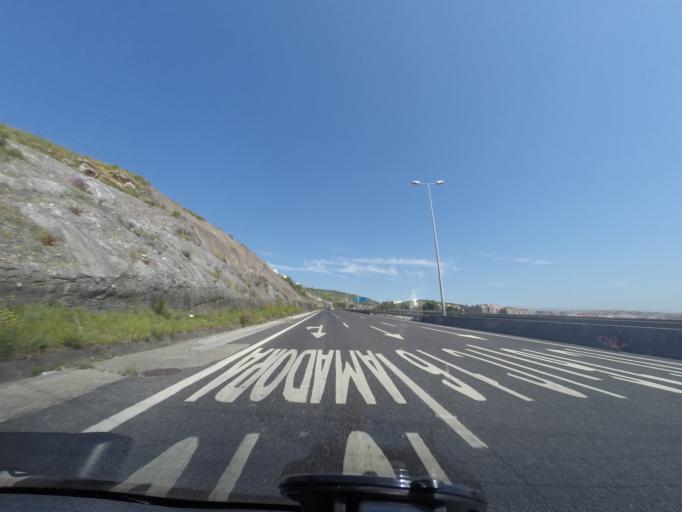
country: PT
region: Lisbon
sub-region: Odivelas
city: Famoes
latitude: 38.7783
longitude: -9.2280
